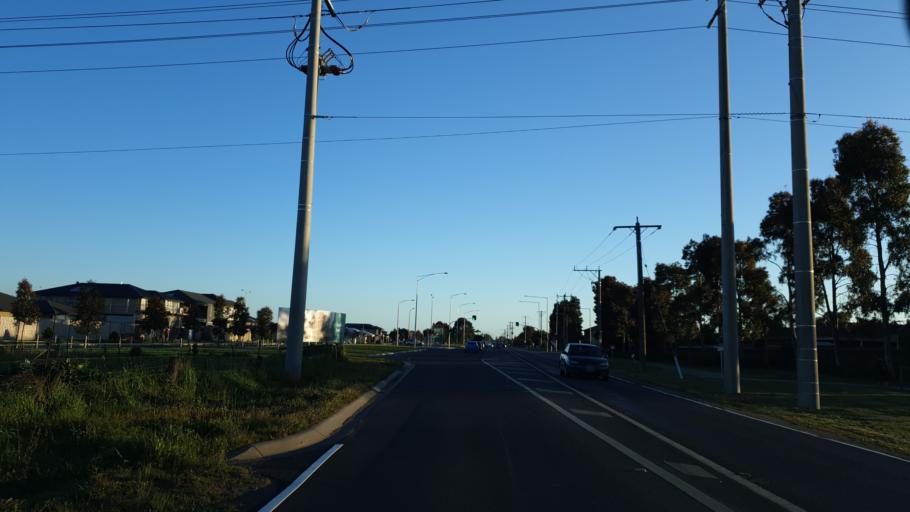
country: AU
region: Victoria
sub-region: Casey
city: Cranbourne
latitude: -38.0914
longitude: 145.2941
